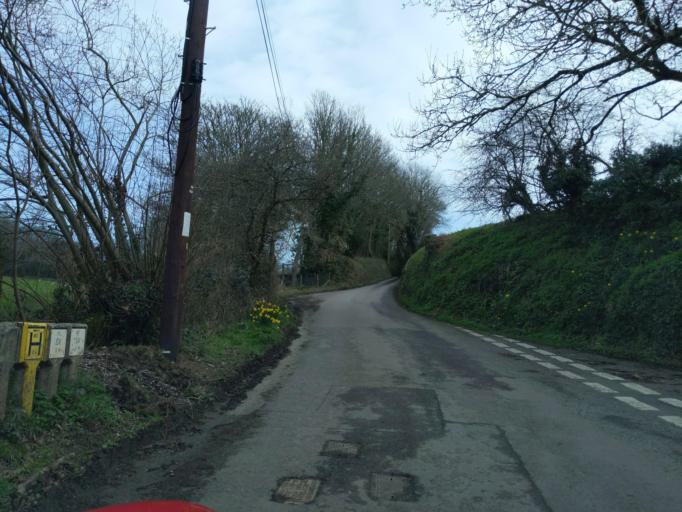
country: GB
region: England
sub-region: Devon
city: Yealmpton
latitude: 50.3640
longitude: -4.0110
